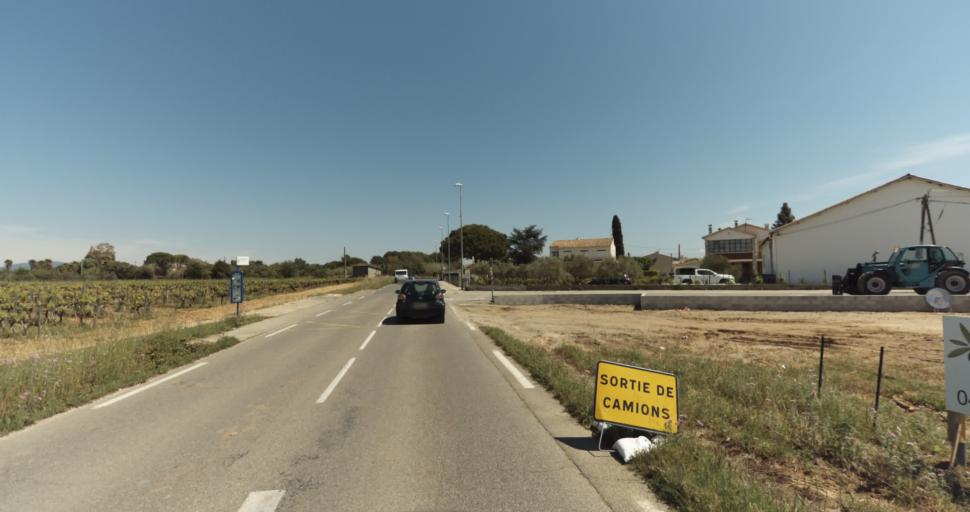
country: FR
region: Provence-Alpes-Cote d'Azur
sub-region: Departement du Var
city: La Crau
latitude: 43.1426
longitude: 6.0615
